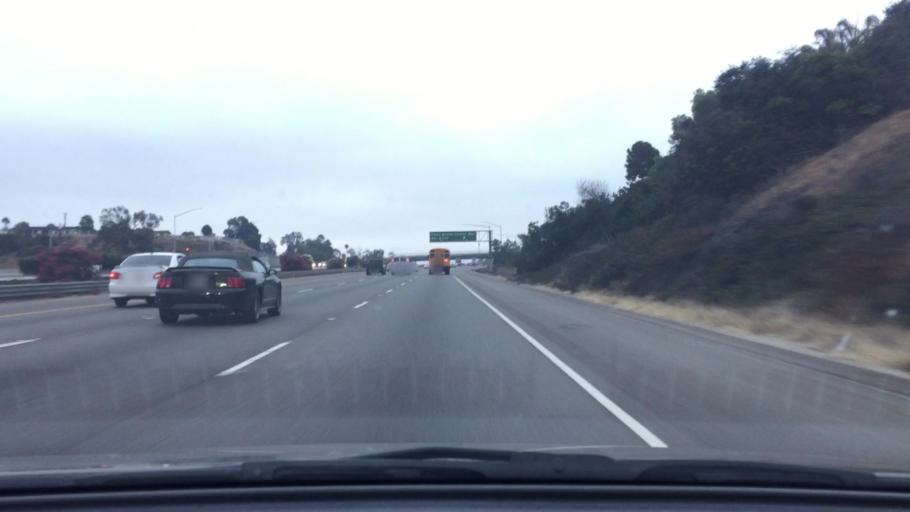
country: US
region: California
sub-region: San Diego County
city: Chula Vista
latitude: 32.6627
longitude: -117.0634
